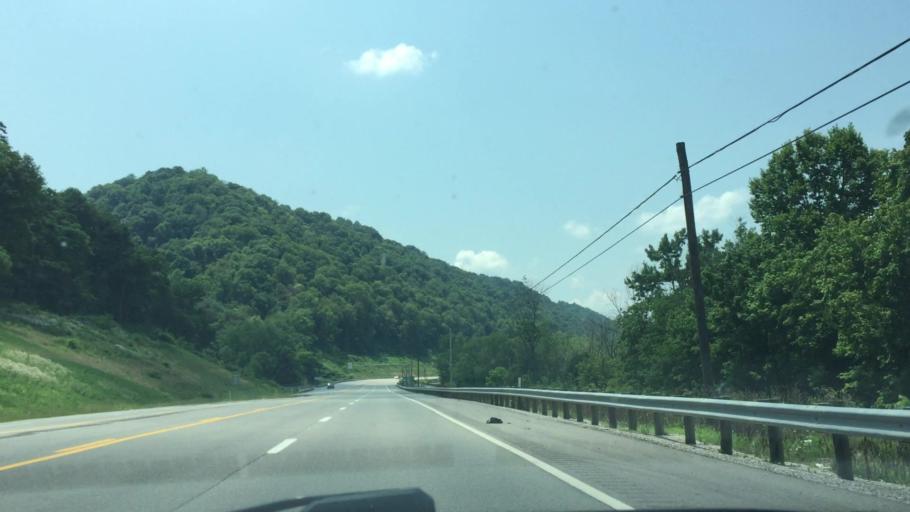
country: US
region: Ohio
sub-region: Belmont County
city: Powhatan Point
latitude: 39.7952
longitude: -80.8233
